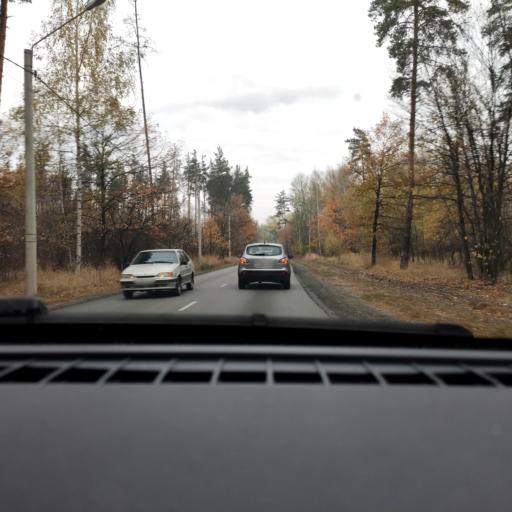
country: RU
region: Voronezj
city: Somovo
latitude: 51.7140
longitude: 39.3257
